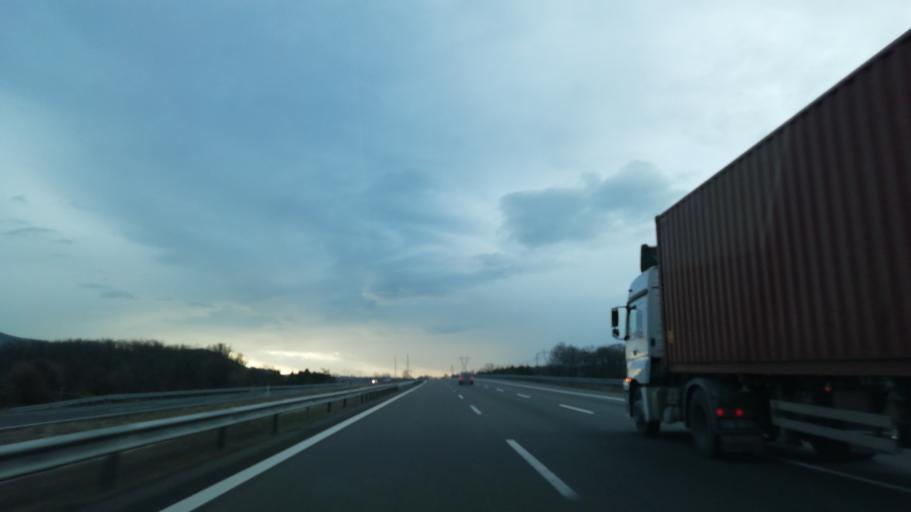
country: TR
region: Bolu
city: Yenicaga
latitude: 40.7535
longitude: 31.9528
